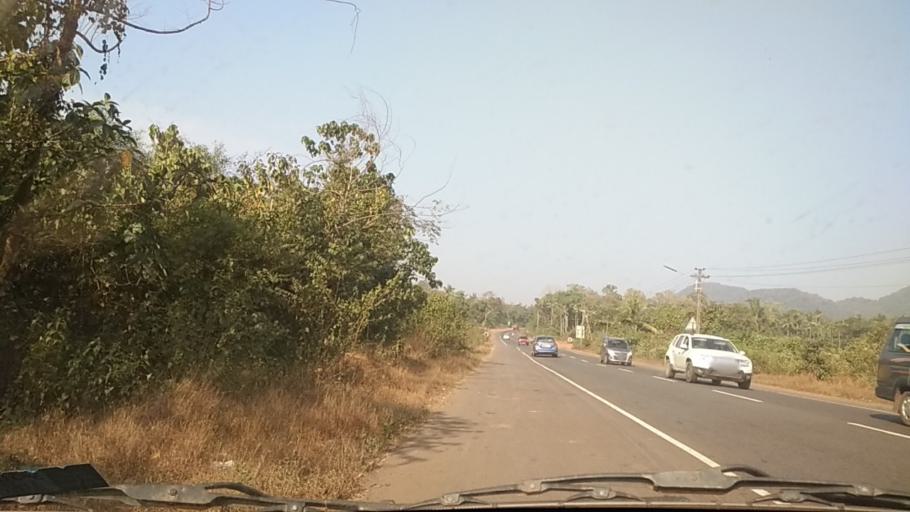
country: IN
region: Goa
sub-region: North Goa
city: Palle
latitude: 15.3893
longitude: 74.1266
